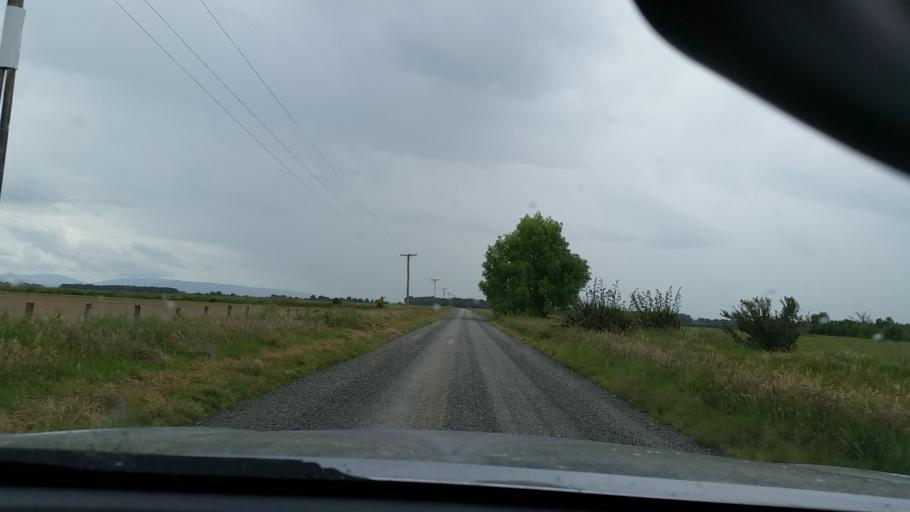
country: NZ
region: Southland
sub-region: Southland District
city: Winton
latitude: -46.0086
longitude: 168.1908
